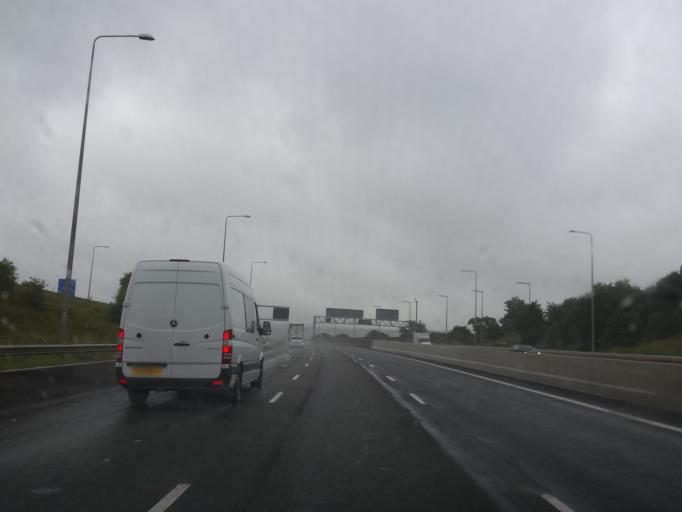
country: GB
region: England
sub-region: Derbyshire
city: Pinxton
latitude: 53.1000
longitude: -1.3217
